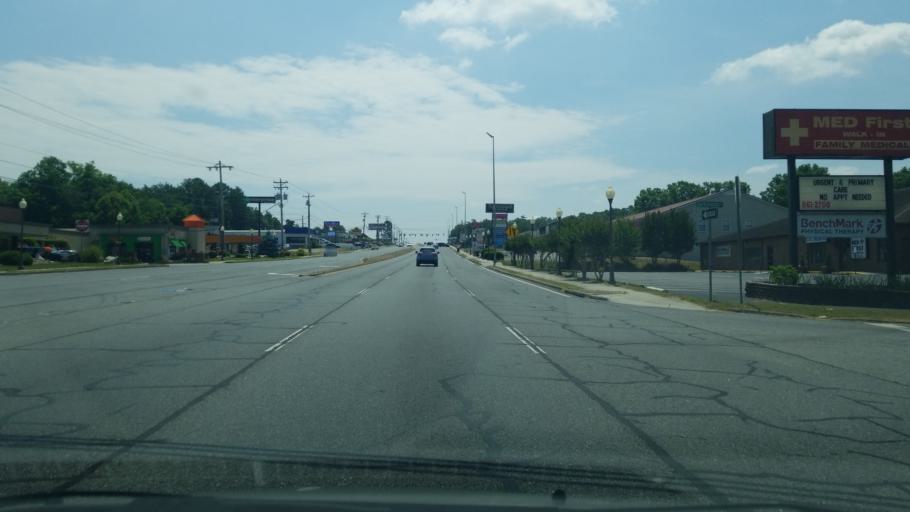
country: US
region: Georgia
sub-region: Catoosa County
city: Fort Oglethorpe
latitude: 34.9516
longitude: -85.2424
